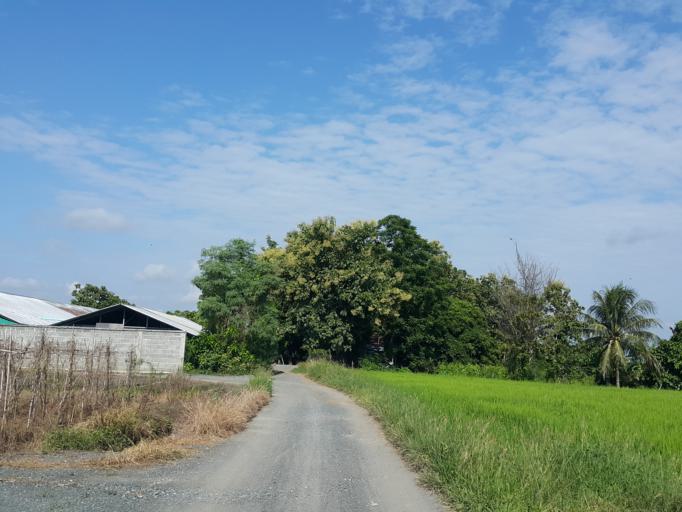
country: TH
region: Chiang Mai
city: San Kamphaeng
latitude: 18.8254
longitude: 99.1627
